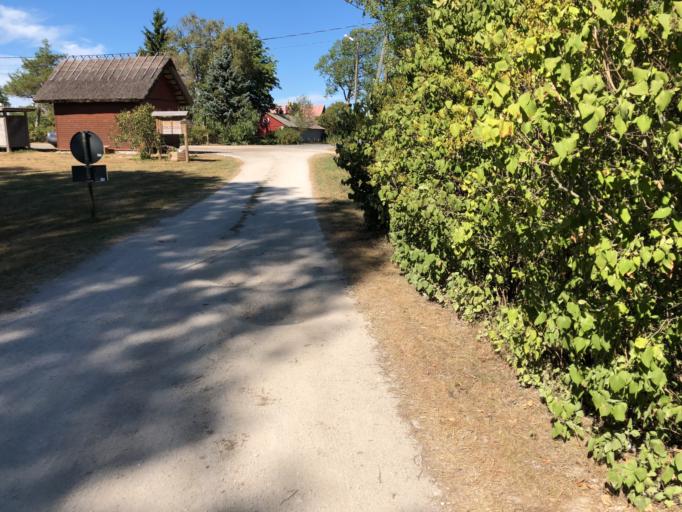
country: EE
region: Laeaene
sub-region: Haapsalu linn
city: Haapsalu
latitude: 58.7729
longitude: 23.5478
